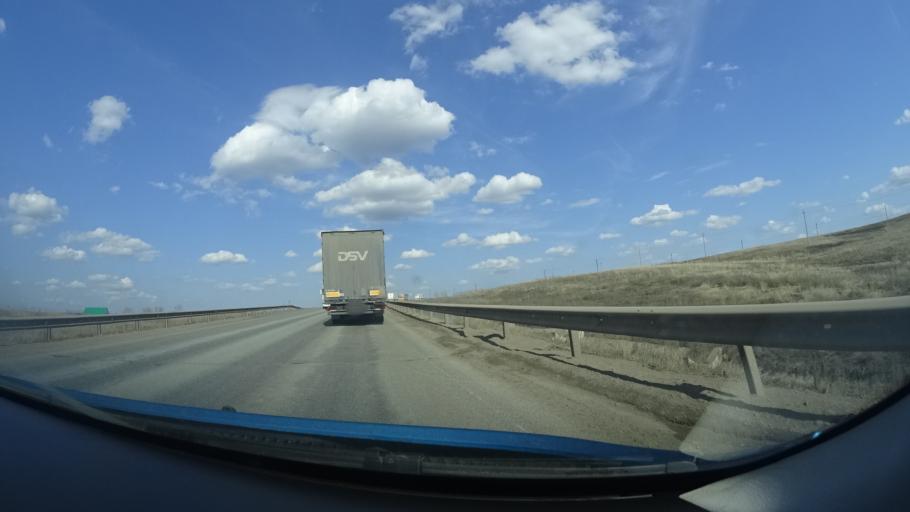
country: RU
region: Bashkortostan
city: Buzdyak
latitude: 54.6679
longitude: 54.7433
